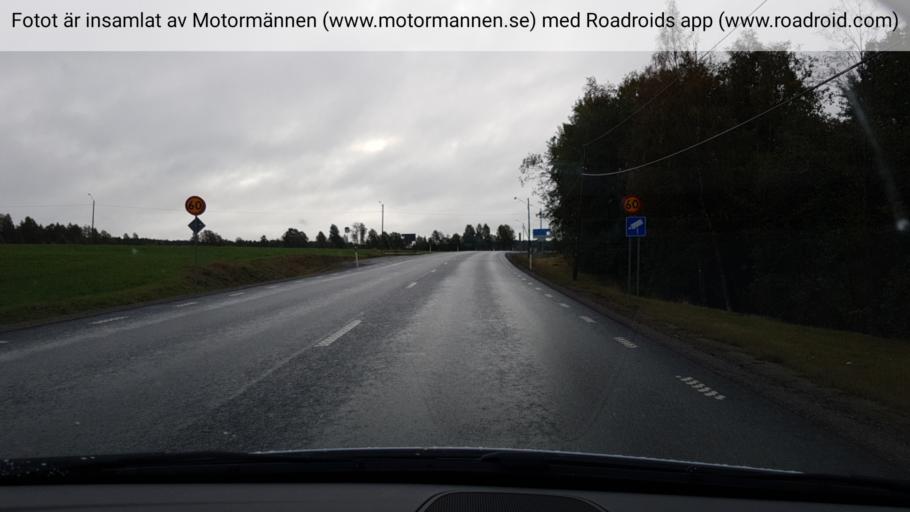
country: SE
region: Vaesterbotten
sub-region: Umea Kommun
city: Roback
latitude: 63.8792
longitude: 20.0513
